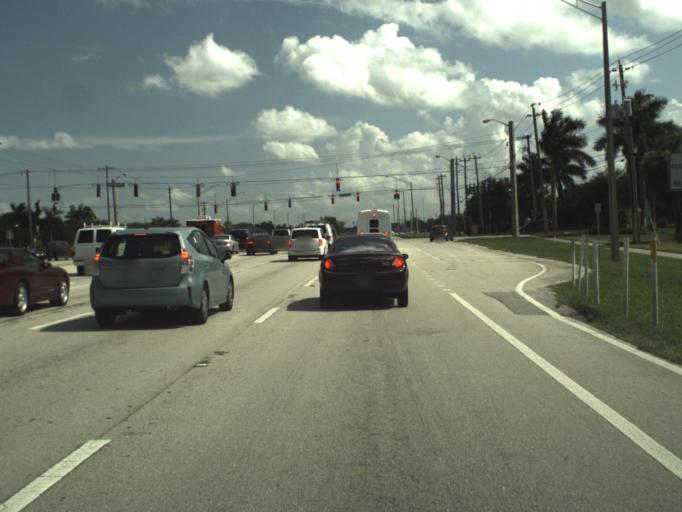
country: US
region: Florida
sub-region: Palm Beach County
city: Royal Palm Beach
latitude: 26.6926
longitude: -80.2018
